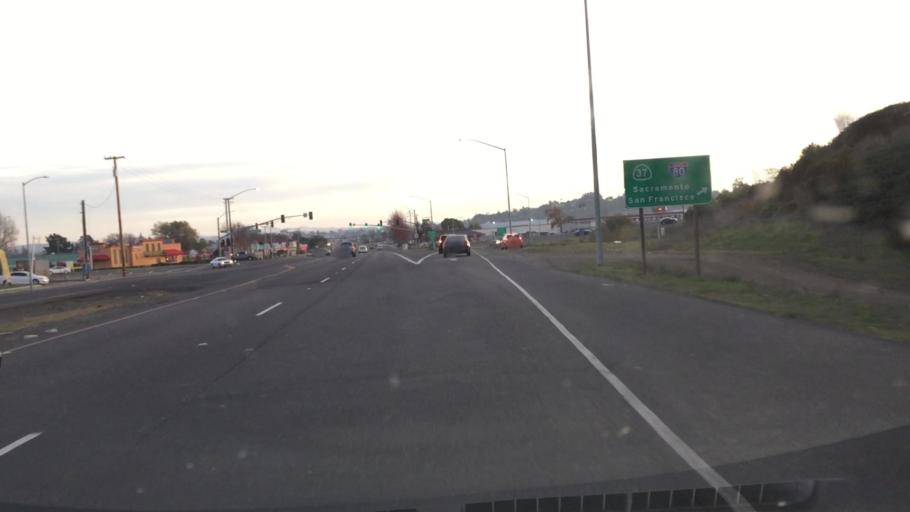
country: US
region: California
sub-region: Solano County
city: Vallejo
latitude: 38.1394
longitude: -122.2562
